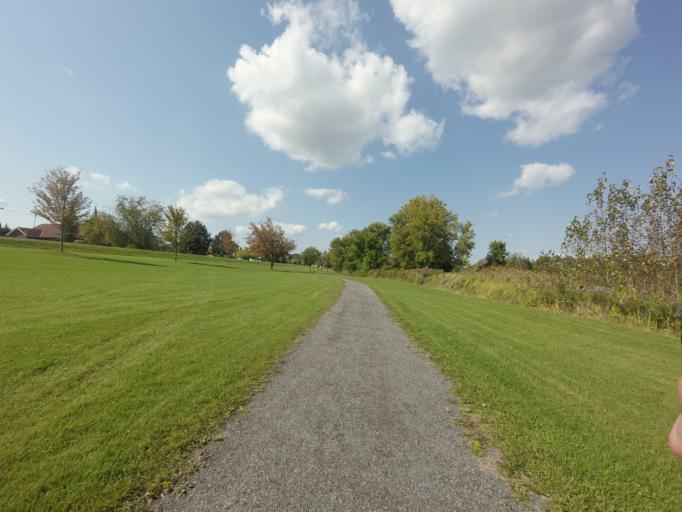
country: CA
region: Ontario
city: Bells Corners
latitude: 45.2379
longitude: -75.6909
